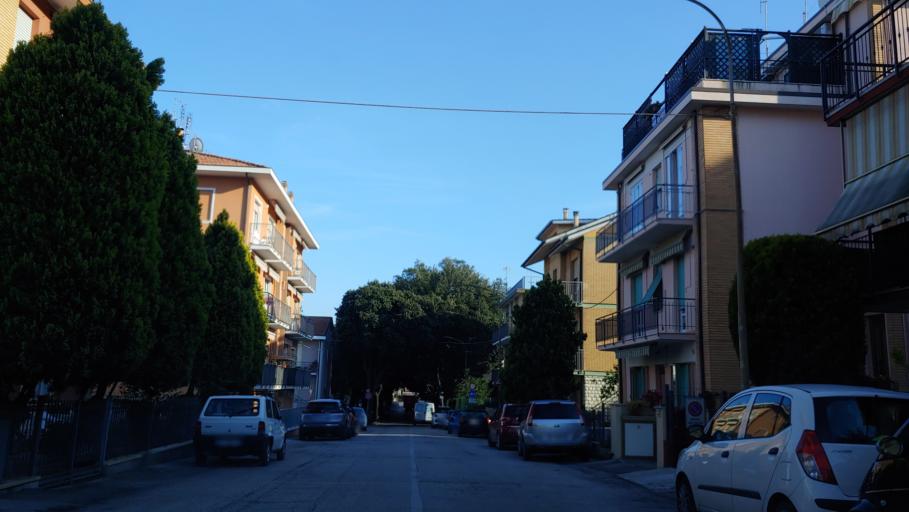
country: IT
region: The Marches
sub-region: Provincia di Pesaro e Urbino
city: Pesaro
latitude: 43.9171
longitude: 12.8989
